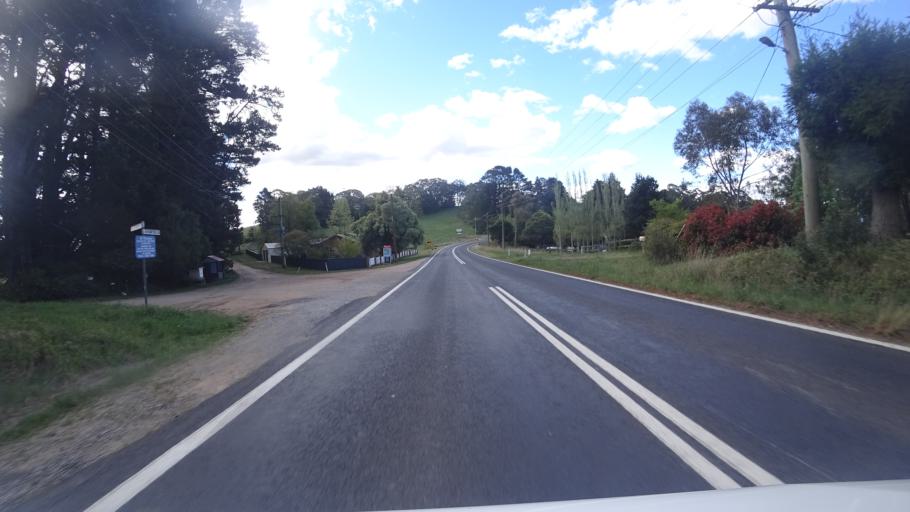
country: AU
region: New South Wales
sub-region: Lithgow
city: Bowenfels
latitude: -33.6458
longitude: 150.0478
